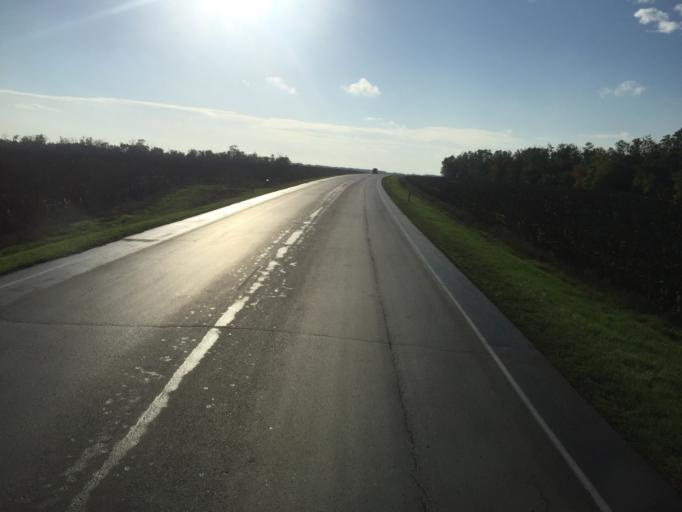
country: RU
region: Rostov
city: Yegorlykskaya
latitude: 46.6541
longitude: 40.5656
